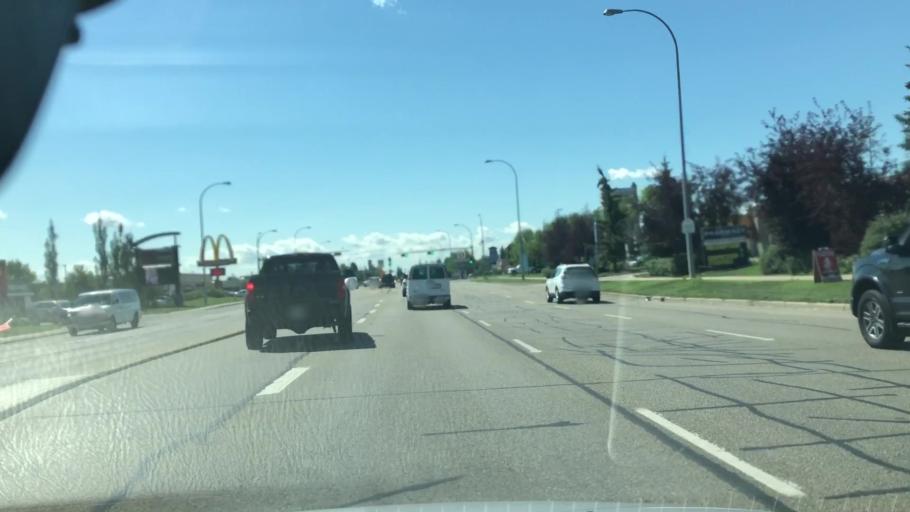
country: CA
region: Alberta
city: Edmonton
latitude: 53.6032
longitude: -113.5411
